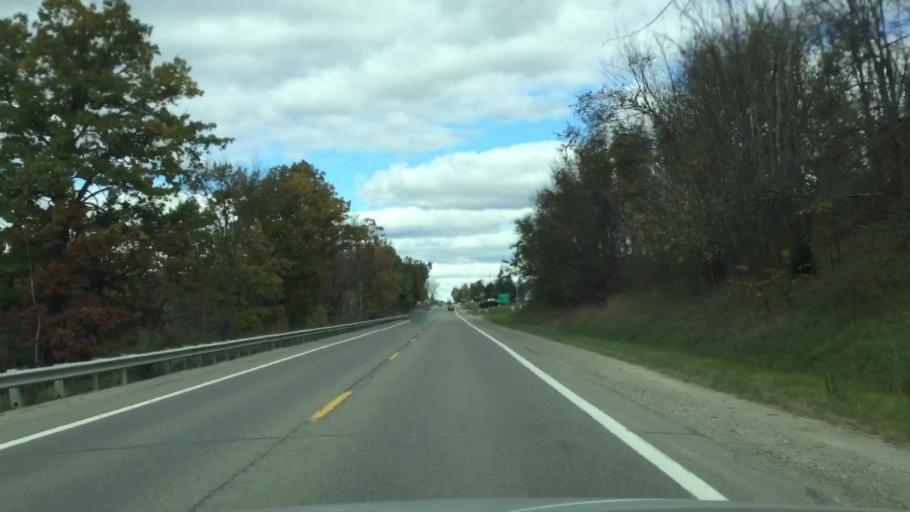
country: US
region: Michigan
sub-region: Lapeer County
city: Barnes Lake-Millers Lake
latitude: 43.1840
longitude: -83.3124
